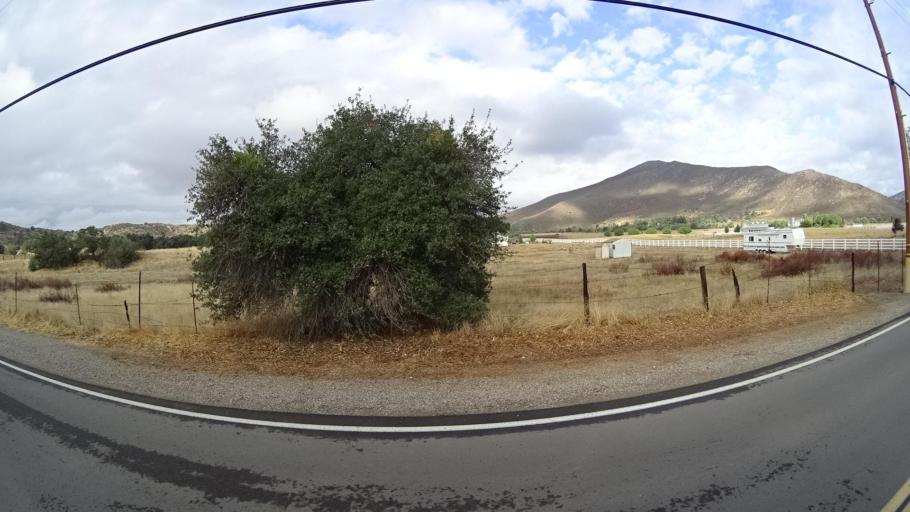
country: MX
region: Baja California
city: Tecate
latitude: 32.6098
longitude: -116.6132
